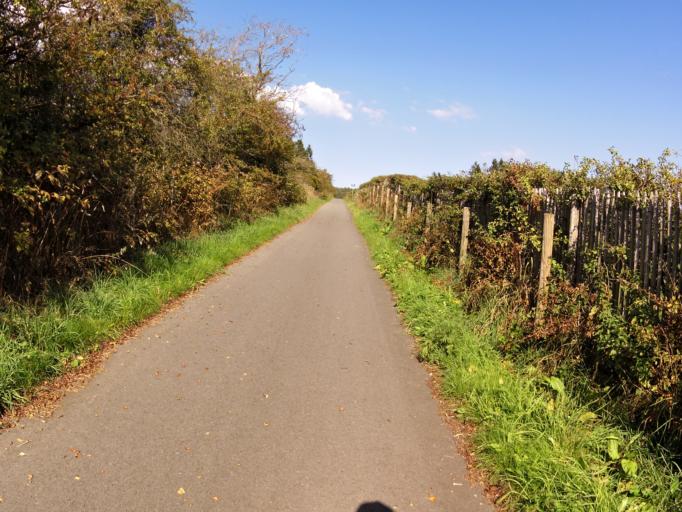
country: BE
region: Wallonia
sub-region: Province de Liege
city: Butgenbach
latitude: 50.4860
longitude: 6.1587
